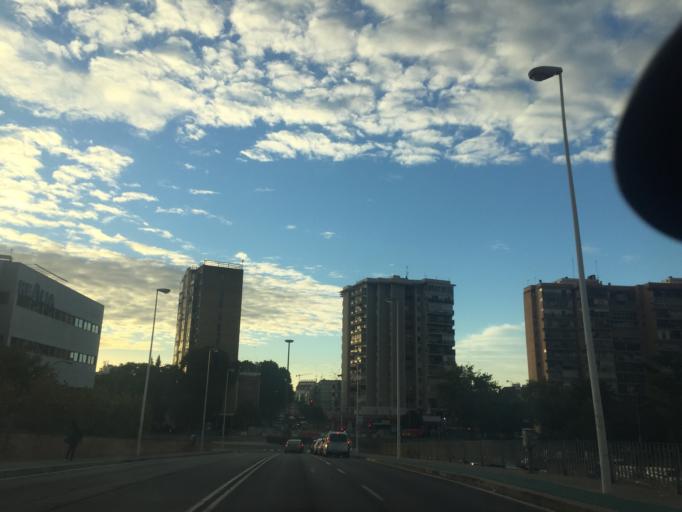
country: ES
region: Andalusia
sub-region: Provincia de Sevilla
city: Sevilla
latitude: 37.3940
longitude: -5.9719
